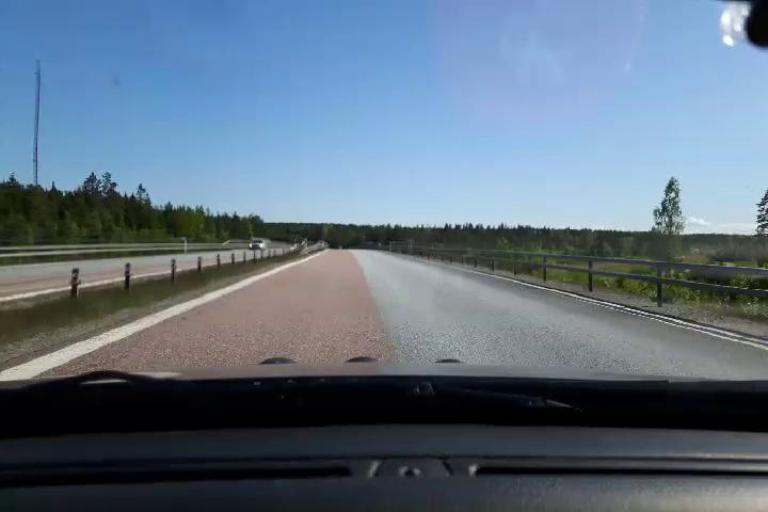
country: SE
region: Gaevleborg
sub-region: Soderhamns Kommun
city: Soderhamn
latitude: 61.3359
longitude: 17.0171
